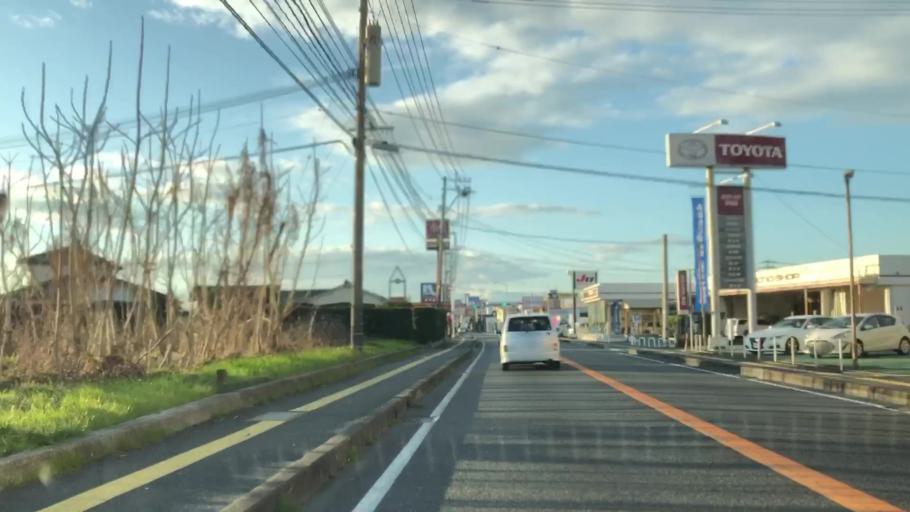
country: JP
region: Oita
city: Bungo-Takada-shi
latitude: 33.5295
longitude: 131.3375
